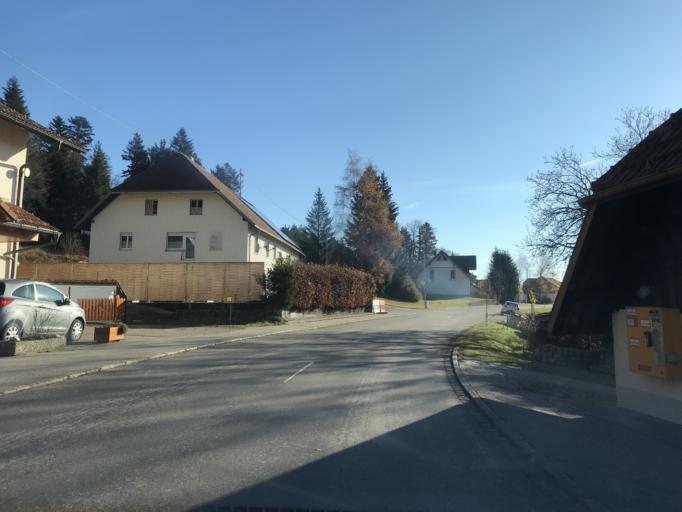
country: DE
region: Baden-Wuerttemberg
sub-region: Freiburg Region
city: Rickenbach
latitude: 47.6393
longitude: 7.9481
